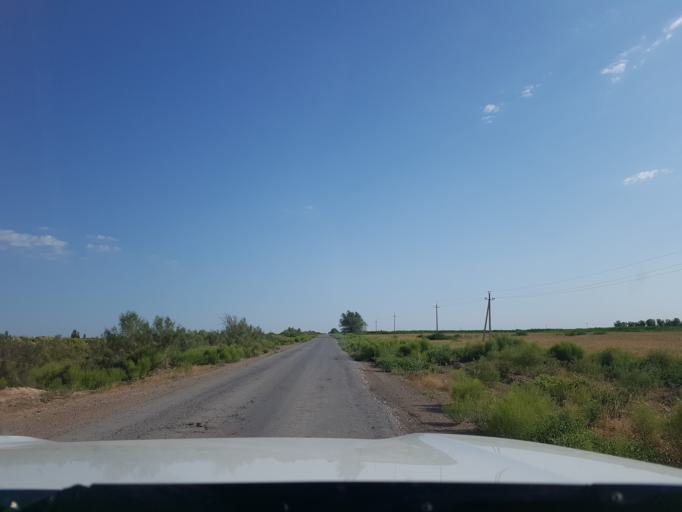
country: TM
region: Dasoguz
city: Koeneuergench
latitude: 41.9117
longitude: 58.7100
